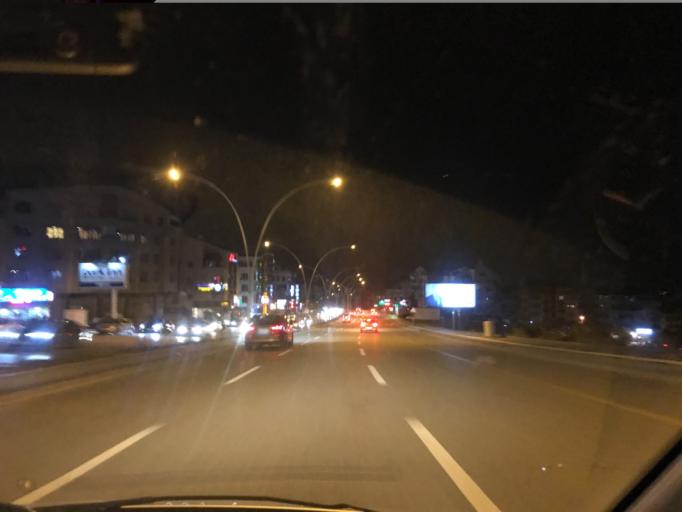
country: TR
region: Ankara
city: Cankaya
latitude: 39.8628
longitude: 32.8546
